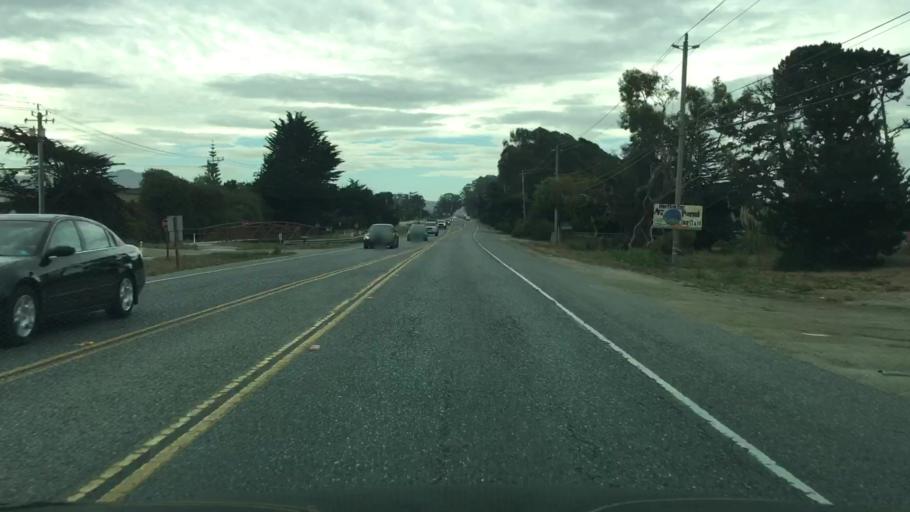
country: US
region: California
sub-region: San Mateo County
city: El Granada
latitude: 37.4904
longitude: -122.4512
